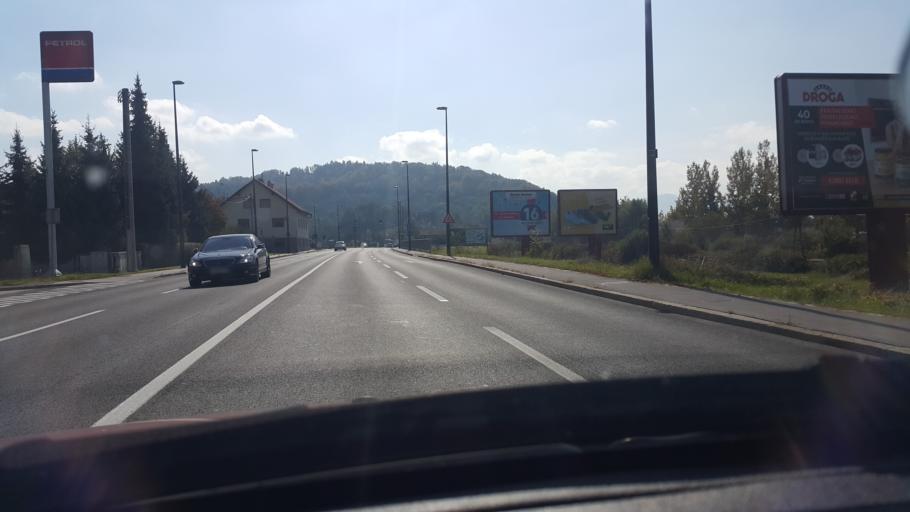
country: SI
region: Skofljica
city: Lavrica
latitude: 46.0197
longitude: 14.5426
